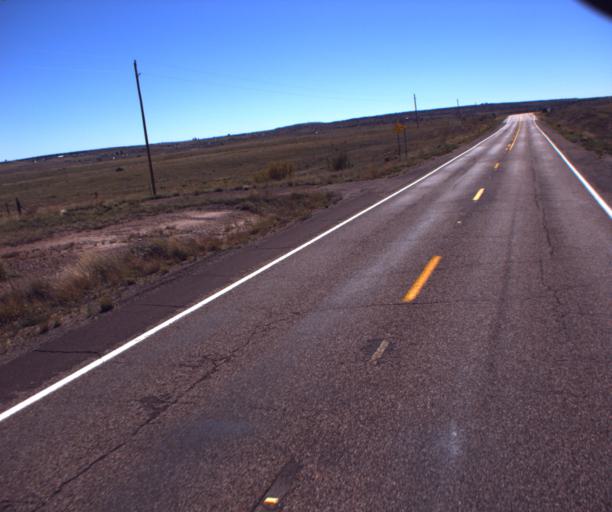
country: US
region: Arizona
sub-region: Apache County
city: Saint Johns
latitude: 34.5155
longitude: -109.4501
